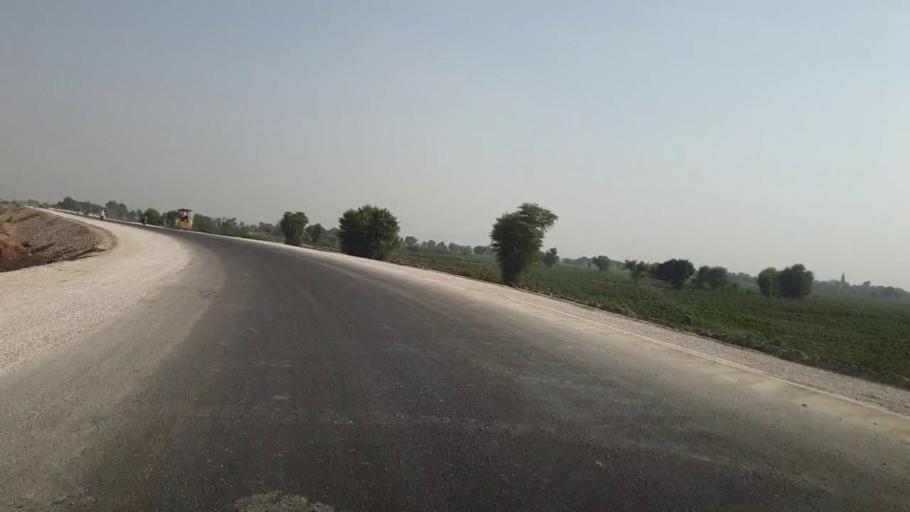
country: PK
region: Sindh
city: Bhan
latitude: 26.5526
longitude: 67.7792
